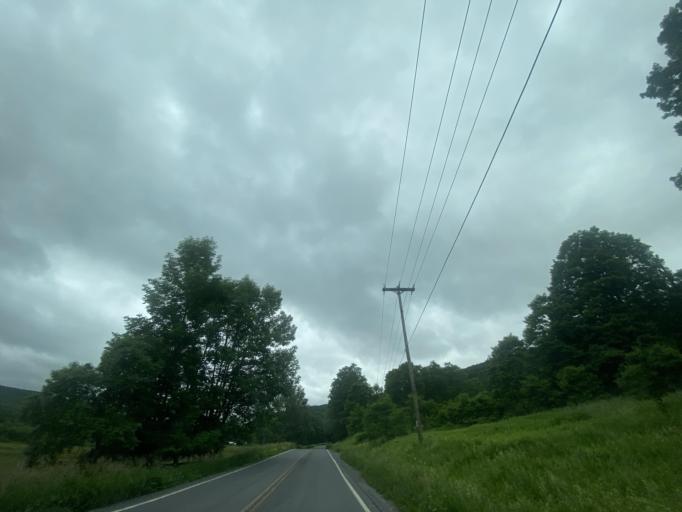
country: US
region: New York
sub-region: Schoharie County
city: Middleburgh
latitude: 42.3895
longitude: -74.3338
